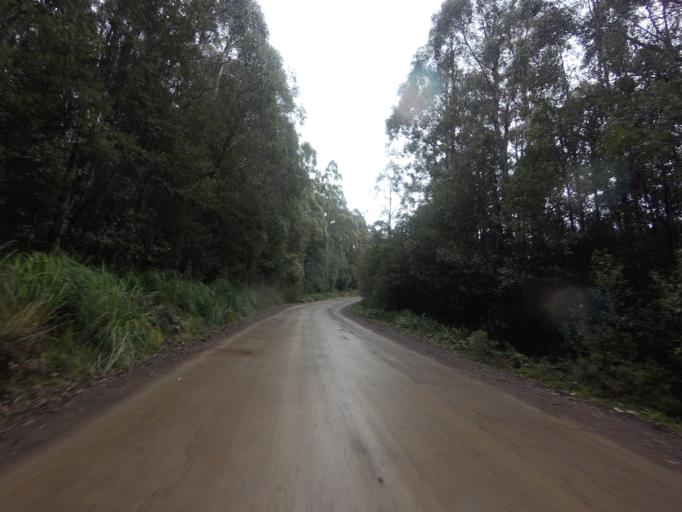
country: AU
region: Tasmania
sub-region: Huon Valley
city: Geeveston
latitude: -43.4793
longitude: 146.8904
